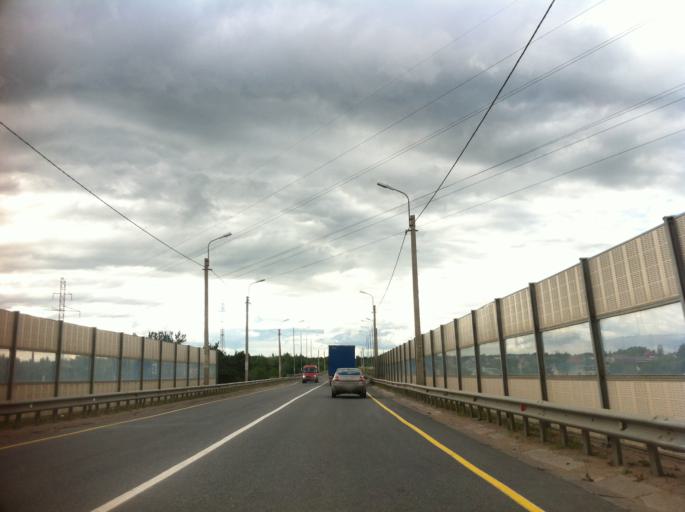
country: RU
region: Pskov
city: Pskov
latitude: 57.8348
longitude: 28.4169
